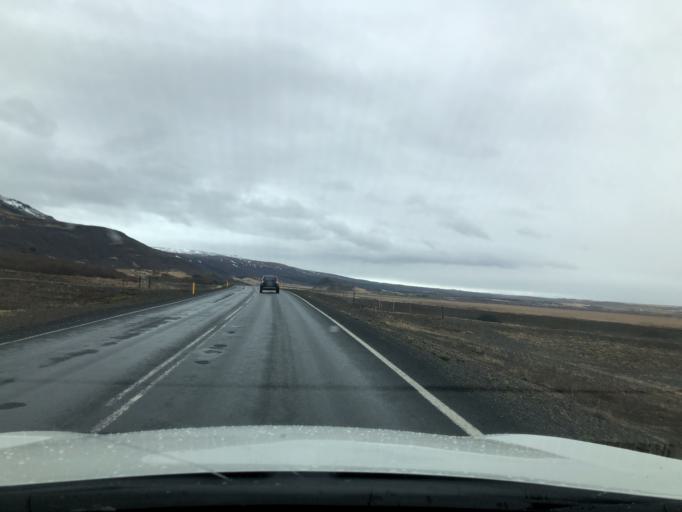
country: IS
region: South
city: Selfoss
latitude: 64.2844
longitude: -20.3413
